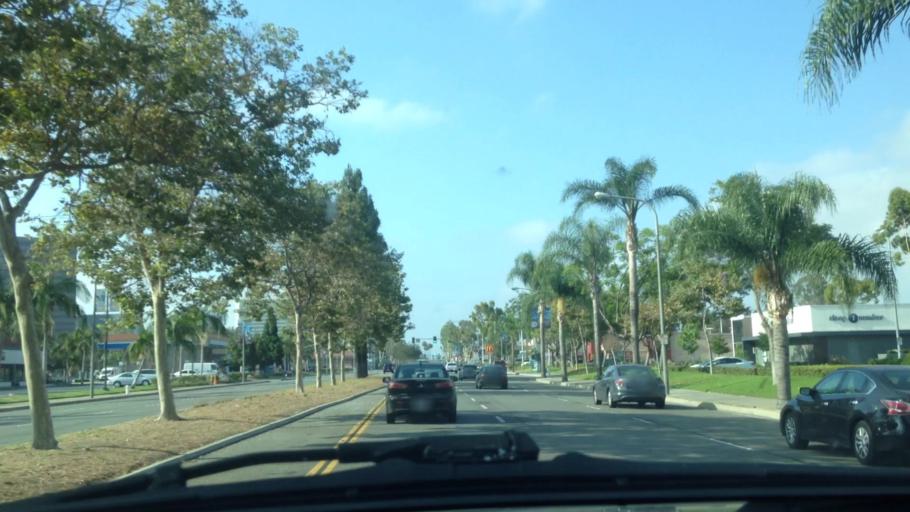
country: US
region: California
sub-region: Orange County
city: Santa Ana
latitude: 33.6986
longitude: -117.8857
